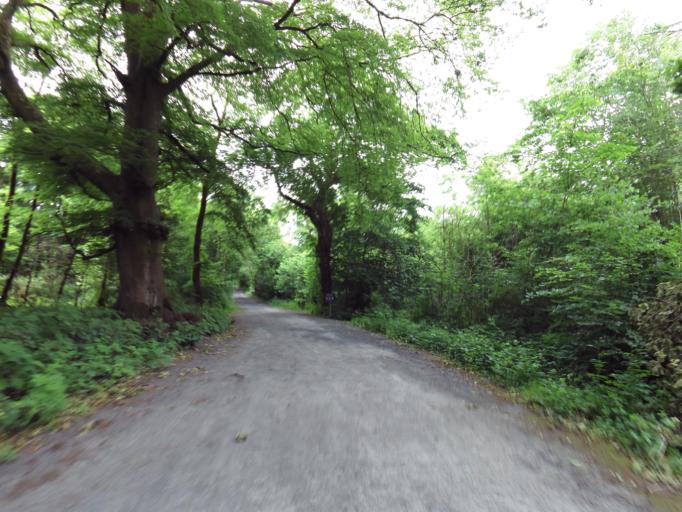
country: IE
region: Connaught
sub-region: County Galway
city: Gort
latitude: 53.0828
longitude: -8.8449
